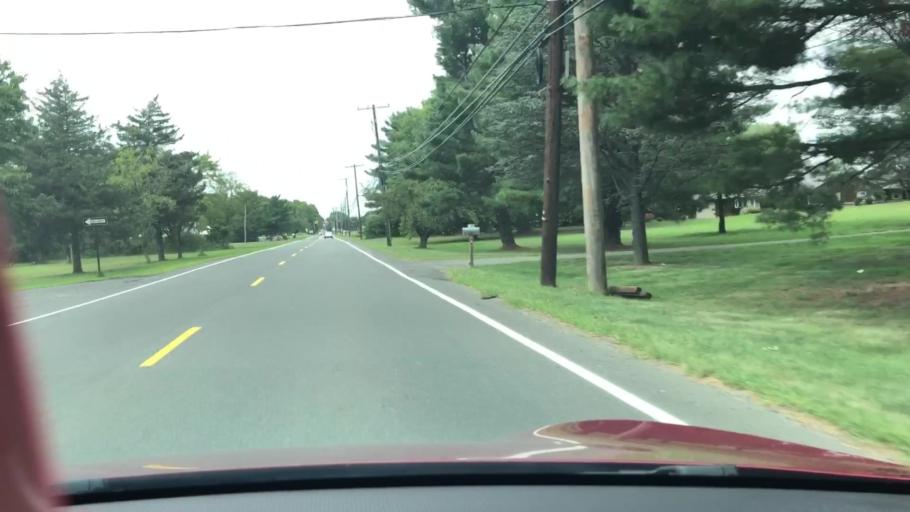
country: US
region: New Jersey
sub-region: Monmouth County
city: Shrewsbury
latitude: 40.1707
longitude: -74.5373
